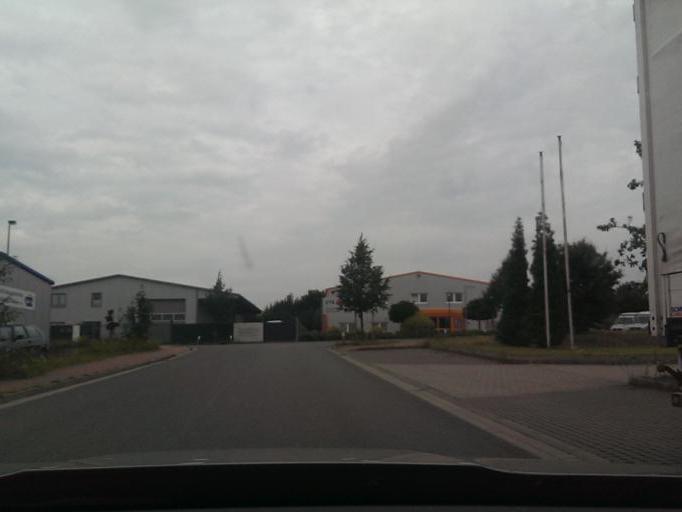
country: DE
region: Lower Saxony
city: Elze
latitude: 52.5172
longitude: 9.7355
